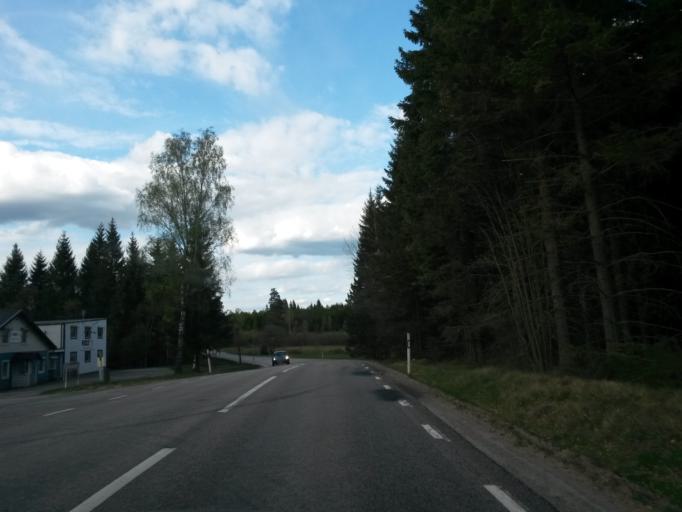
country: SE
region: Vaestra Goetaland
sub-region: Svenljunga Kommun
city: Svenljunga
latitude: 57.5965
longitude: 13.1265
